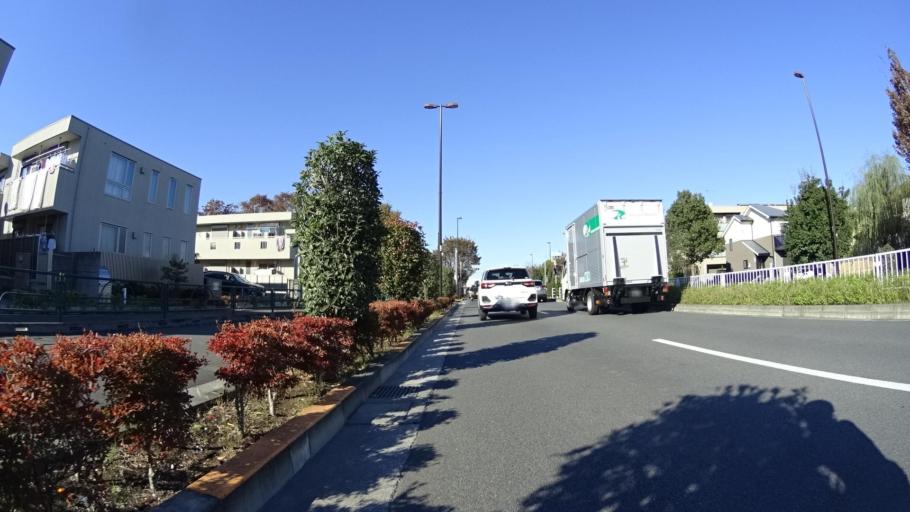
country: JP
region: Tokyo
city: Kamirenjaku
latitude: 35.7000
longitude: 139.5503
